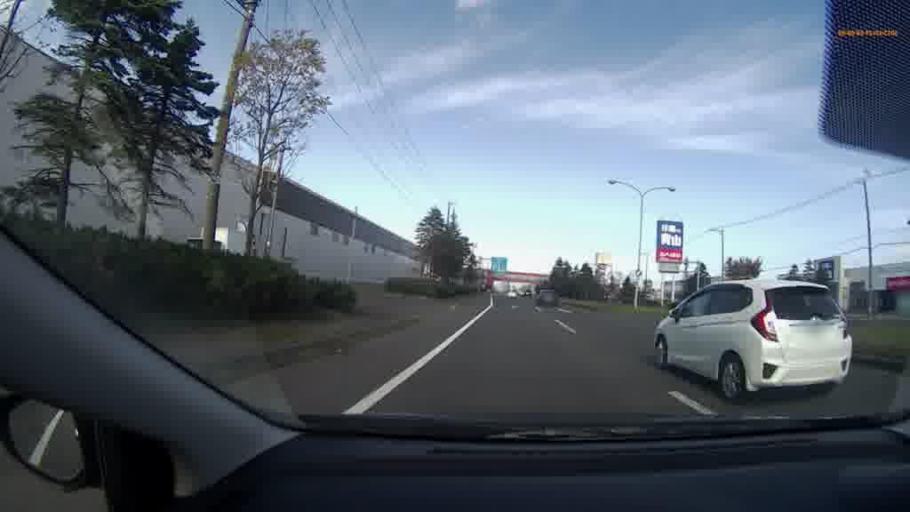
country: JP
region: Hokkaido
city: Kushiro
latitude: 43.0095
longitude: 144.4113
